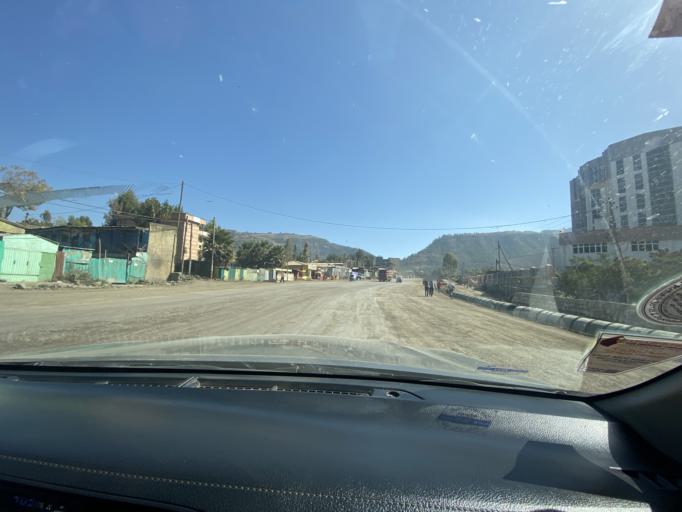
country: ET
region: Amhara
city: Robit
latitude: 11.8262
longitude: 39.5928
